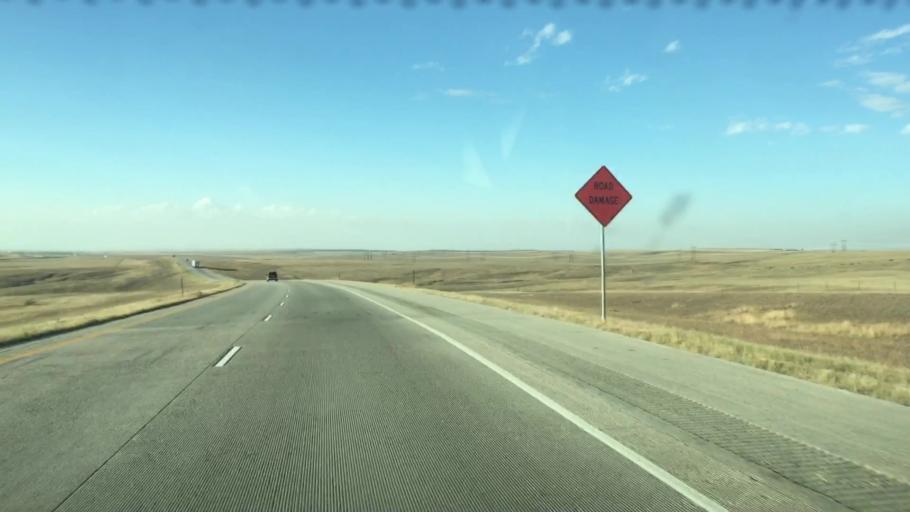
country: US
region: Colorado
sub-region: Lincoln County
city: Limon
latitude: 39.3949
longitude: -103.8902
